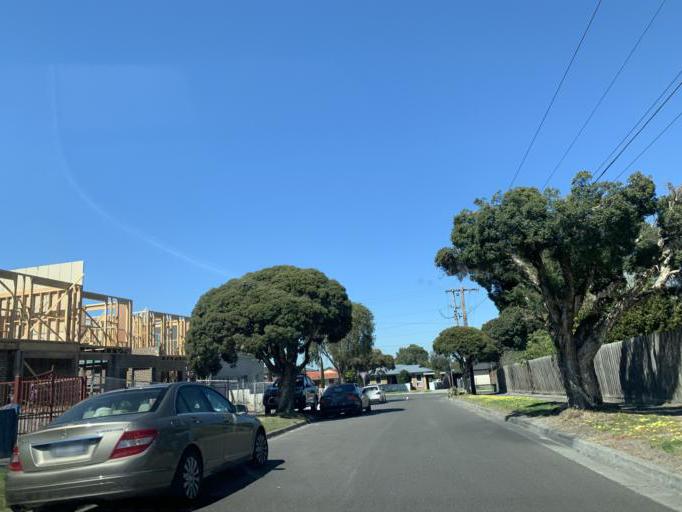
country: AU
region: Victoria
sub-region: Greater Dandenong
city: Dandenong
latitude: -37.9975
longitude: 145.2028
